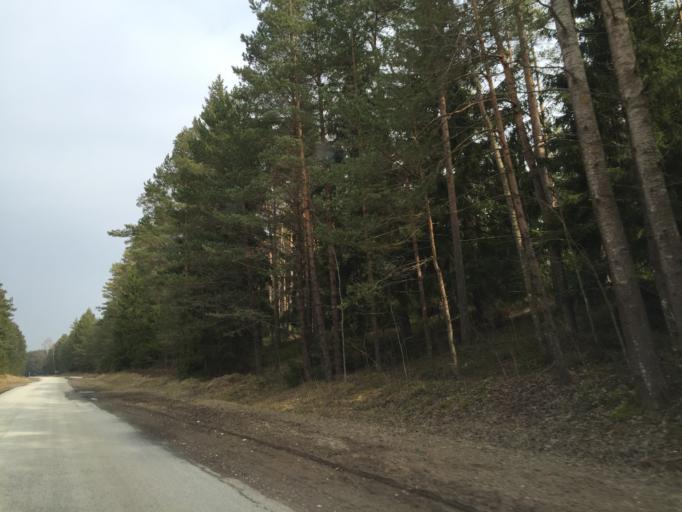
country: LV
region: Salacgrivas
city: Ainazi
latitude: 57.9622
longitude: 24.4050
